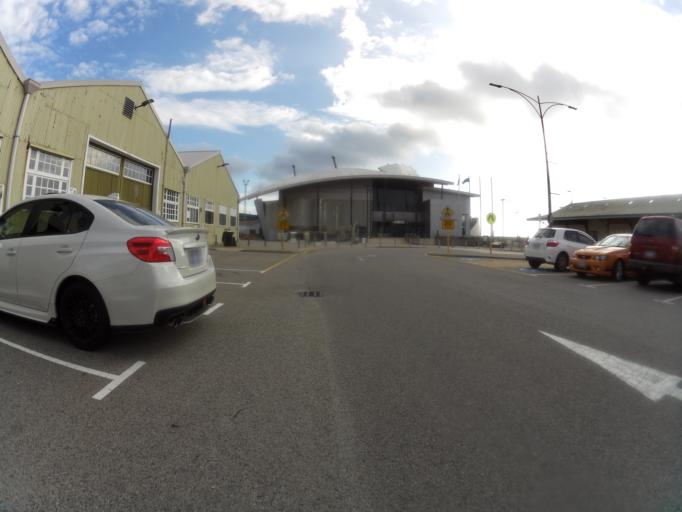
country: AU
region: Western Australia
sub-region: Fremantle
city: South Fremantle
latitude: -32.0545
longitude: 115.7402
